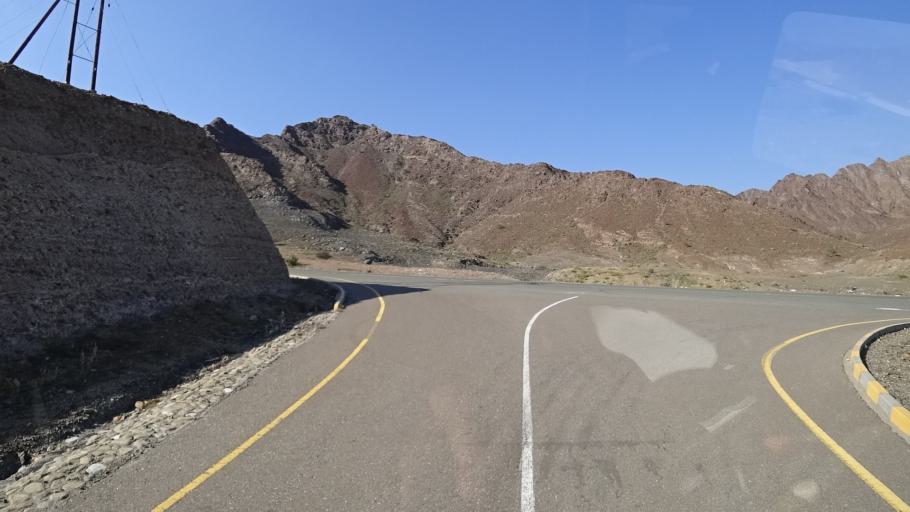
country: OM
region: Al Batinah
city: Rustaq
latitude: 23.4589
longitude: 57.0815
